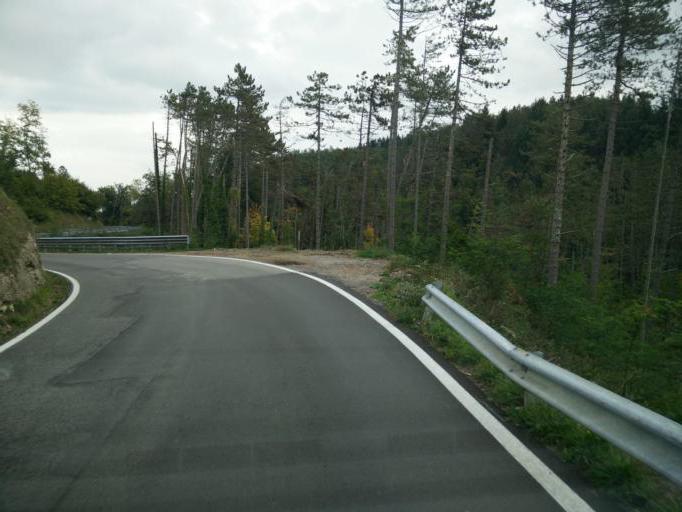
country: IT
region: Tuscany
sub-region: Provincia di Lucca
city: Giuncugnano
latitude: 44.2018
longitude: 10.2326
